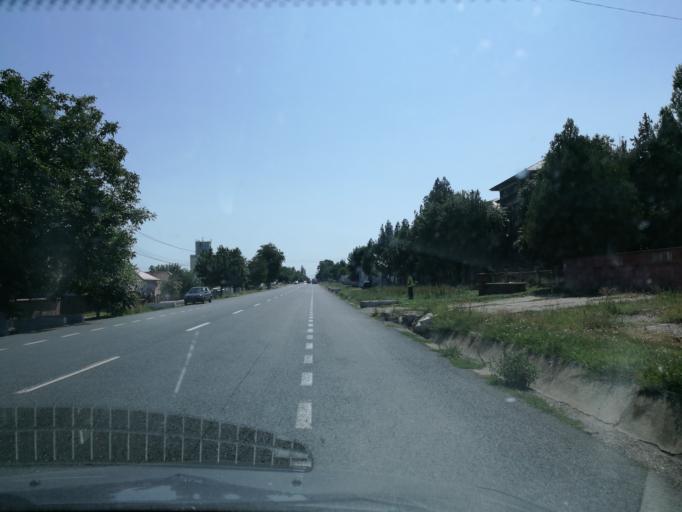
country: RO
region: Bacau
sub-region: Comuna Sascut
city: Sascut
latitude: 46.2114
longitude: 27.1060
